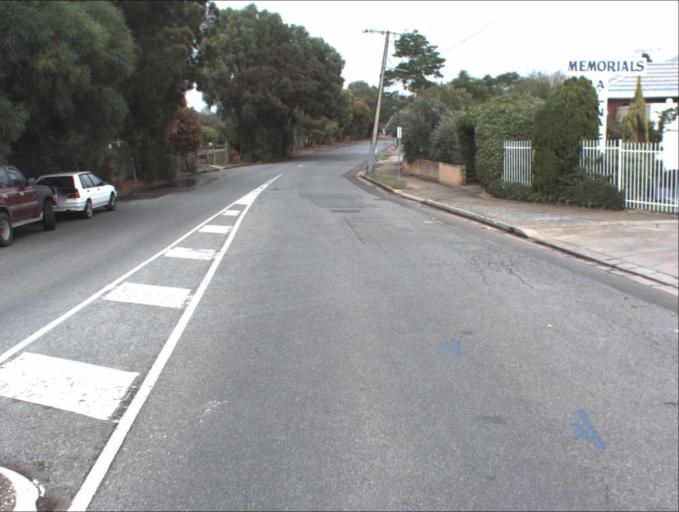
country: AU
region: South Australia
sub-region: Prospect
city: Prospect
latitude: -34.8852
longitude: 138.5830
